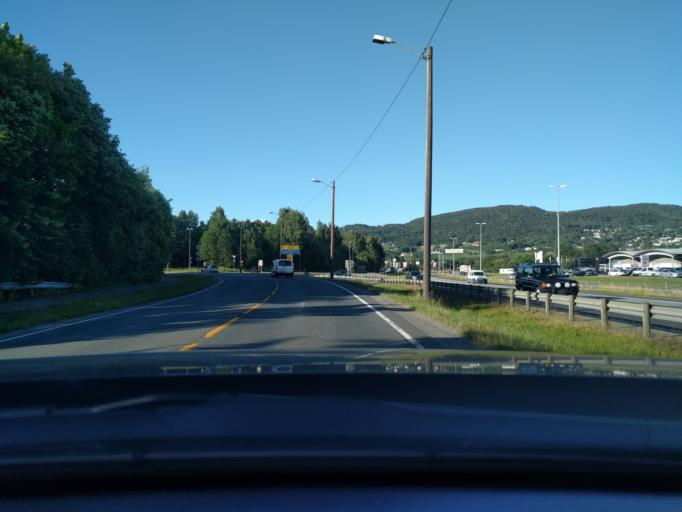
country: NO
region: Buskerud
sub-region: Lier
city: Lierbyen
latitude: 59.7672
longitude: 10.2564
